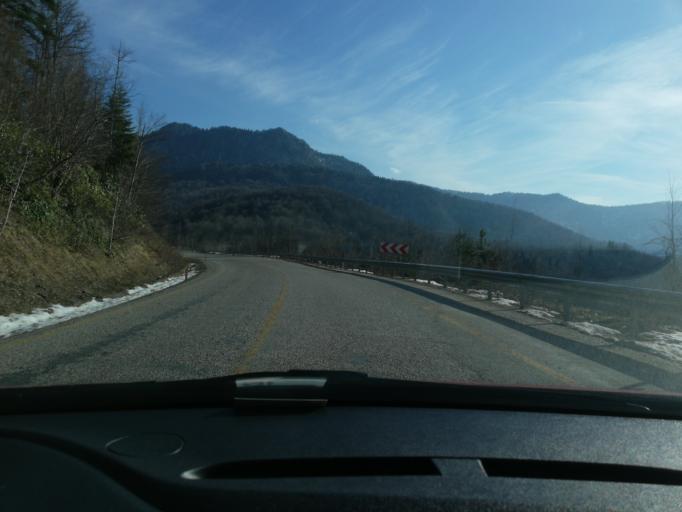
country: TR
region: Kastamonu
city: Senpazar
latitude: 41.7953
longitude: 33.1161
